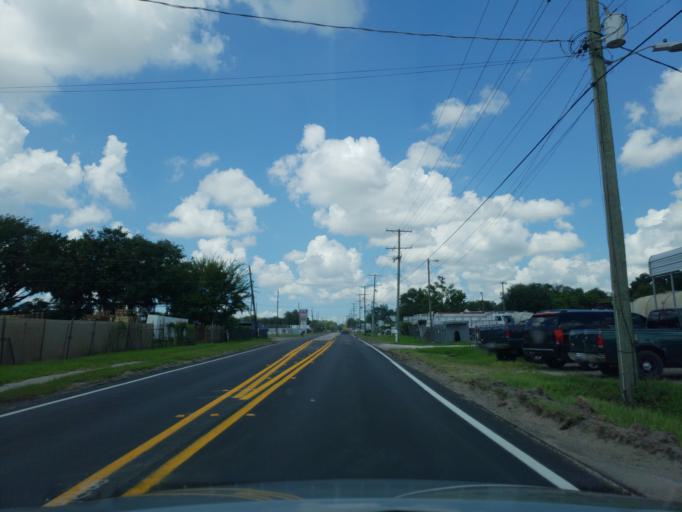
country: US
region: Florida
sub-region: Hillsborough County
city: East Lake-Orient Park
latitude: 27.9668
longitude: -82.3774
